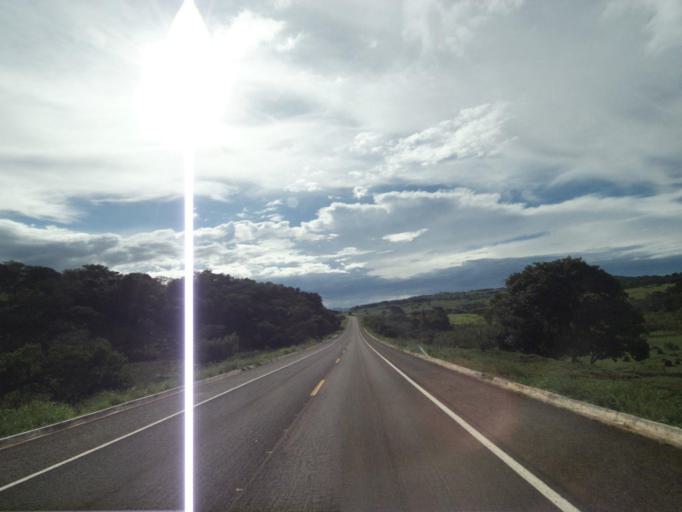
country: BR
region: Goias
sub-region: Jaragua
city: Jaragua
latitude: -15.8936
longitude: -49.5070
